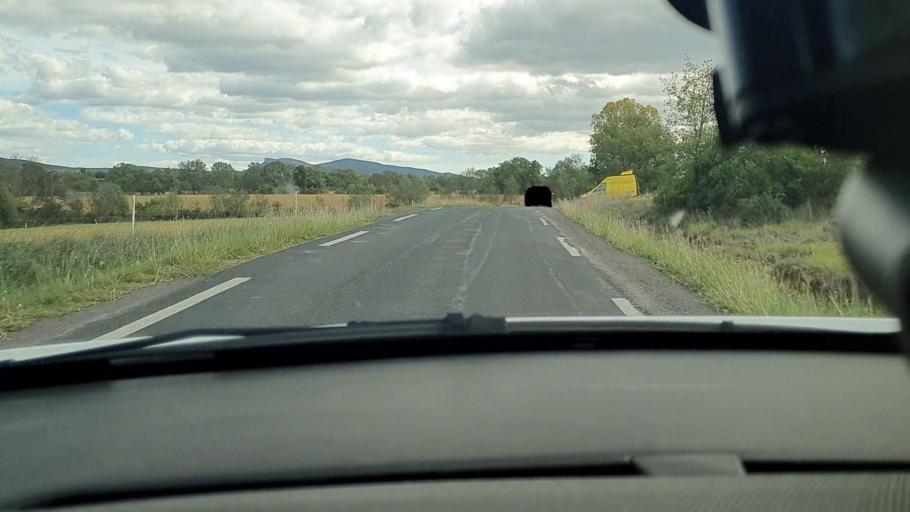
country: FR
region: Languedoc-Roussillon
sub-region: Departement du Gard
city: Les Mages
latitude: 44.1999
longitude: 4.2097
